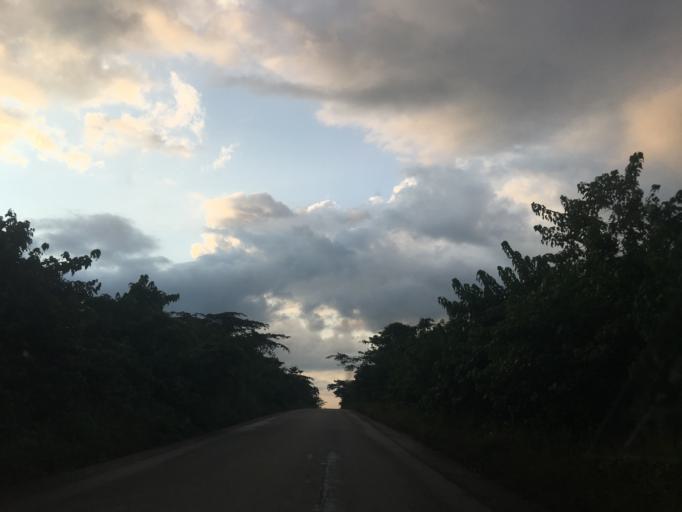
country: GH
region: Western
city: Bibiani
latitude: 6.7695
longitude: -2.5106
